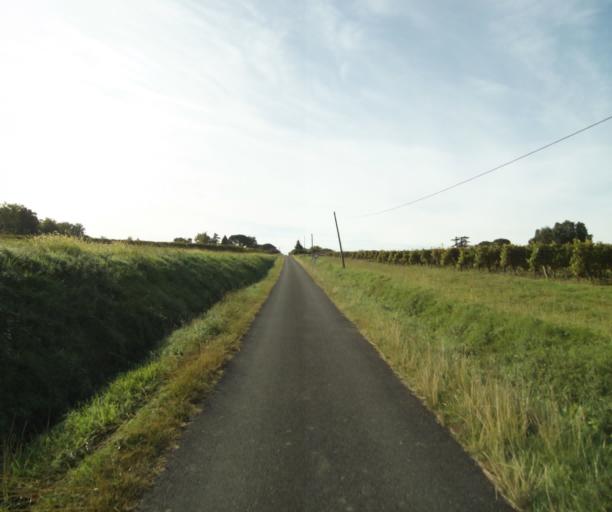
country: FR
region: Midi-Pyrenees
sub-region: Departement du Gers
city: Eauze
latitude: 43.9356
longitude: 0.1181
